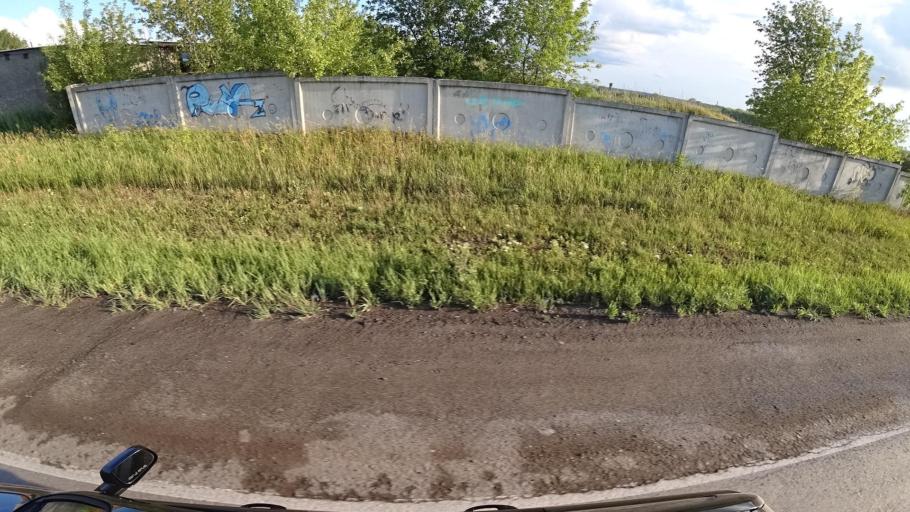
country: RU
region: Sverdlovsk
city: Kamyshlov
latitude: 56.8574
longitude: 62.7281
